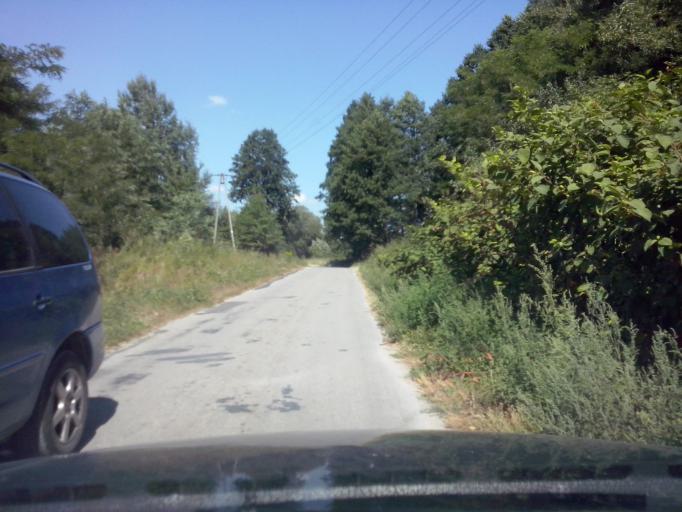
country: PL
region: Swietokrzyskie
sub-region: Powiat buski
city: Gnojno
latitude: 50.6122
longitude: 20.8898
